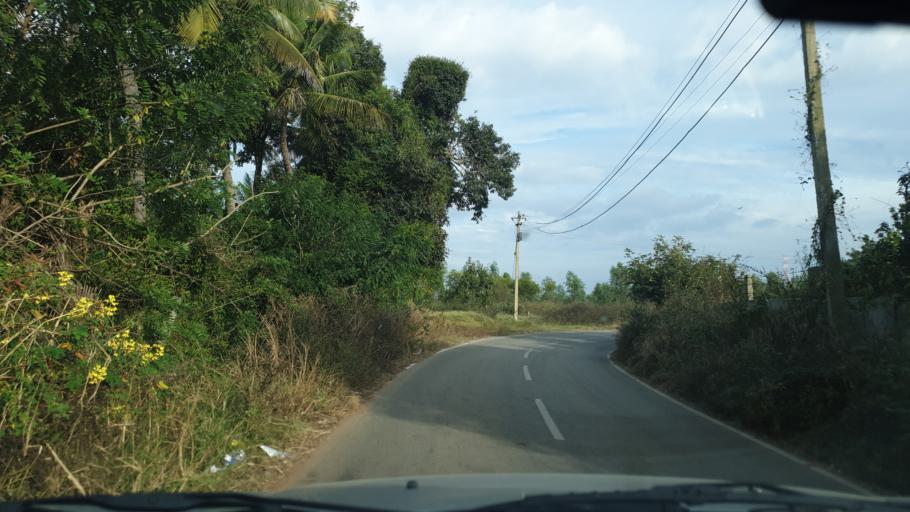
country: IN
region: Karnataka
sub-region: Bangalore Urban
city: Yelahanka
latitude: 13.2012
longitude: 77.6100
